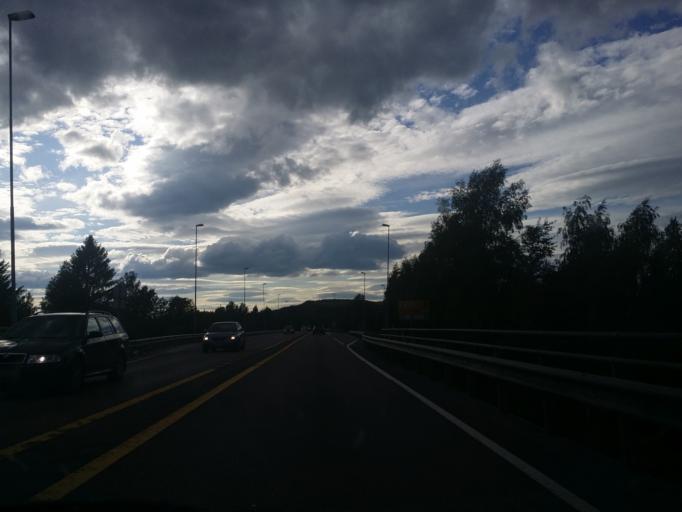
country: NO
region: Hedmark
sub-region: Ringsaker
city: Brumunddal
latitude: 60.8777
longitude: 10.9323
